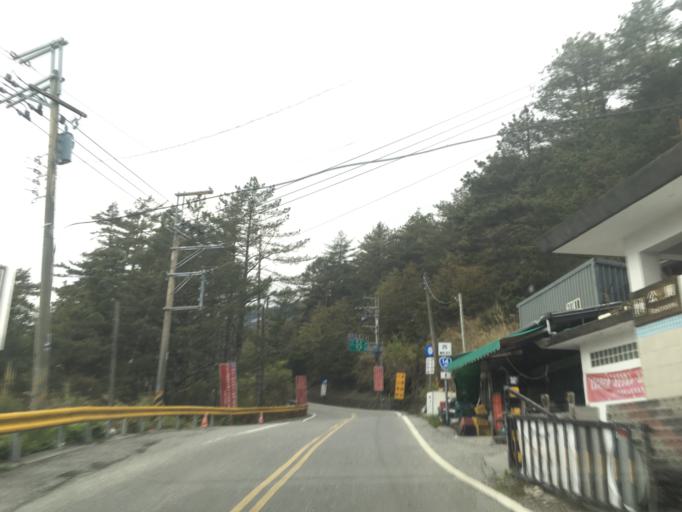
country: TW
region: Taiwan
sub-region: Hualien
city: Hualian
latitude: 24.1806
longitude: 121.3097
